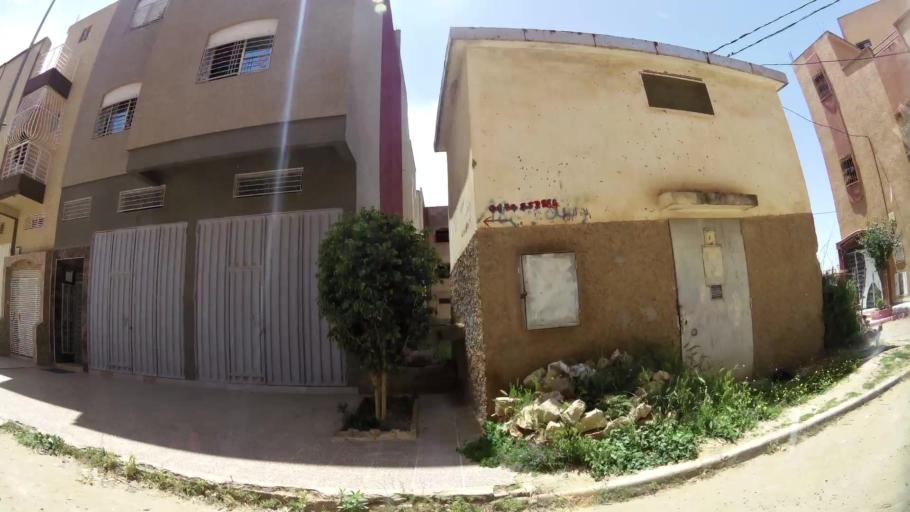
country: MA
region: Rabat-Sale-Zemmour-Zaer
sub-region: Khemisset
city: Khemisset
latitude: 33.8252
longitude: -6.0844
